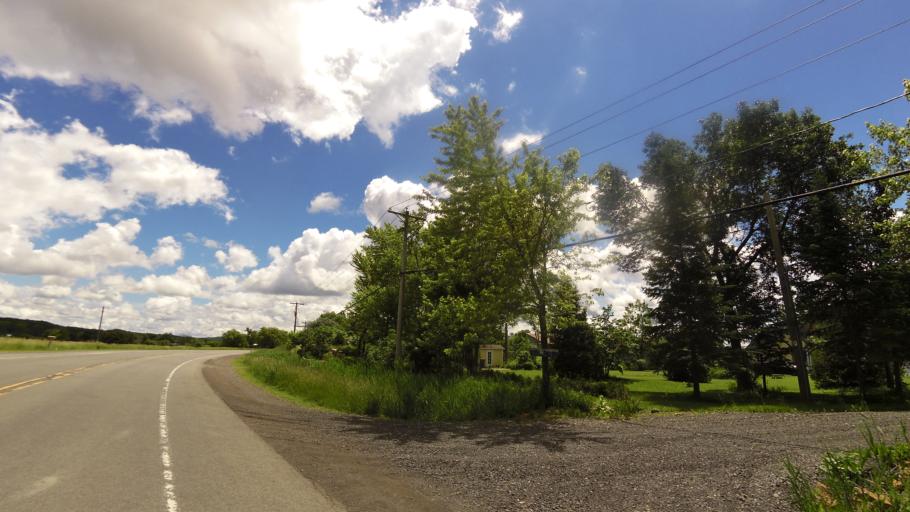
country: CA
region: Quebec
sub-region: Monteregie
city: Hudson
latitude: 45.5308
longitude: -74.1828
